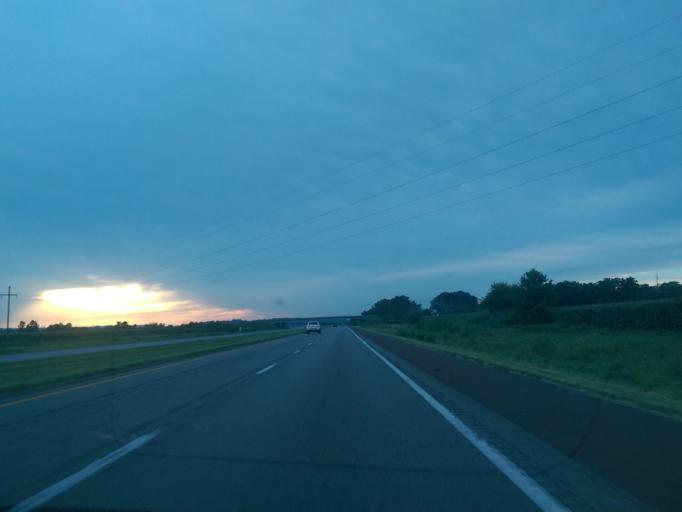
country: US
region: Missouri
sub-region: Holt County
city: Mound City
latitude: 40.1769
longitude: -95.3086
